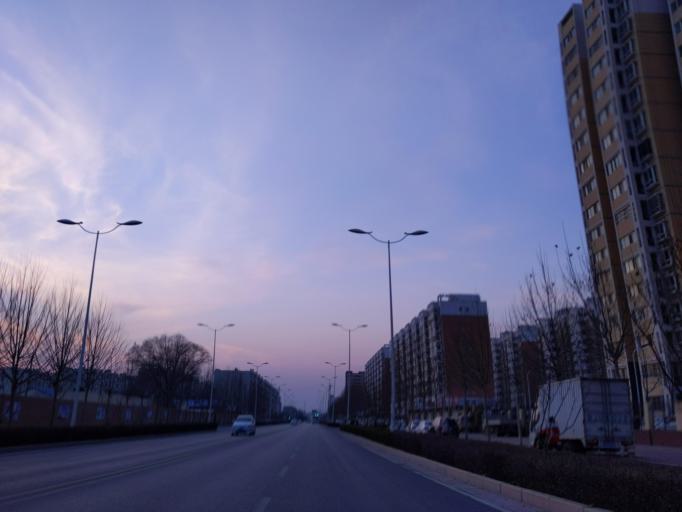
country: CN
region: Henan Sheng
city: Zhongyuanlu
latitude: 35.7755
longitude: 115.1055
